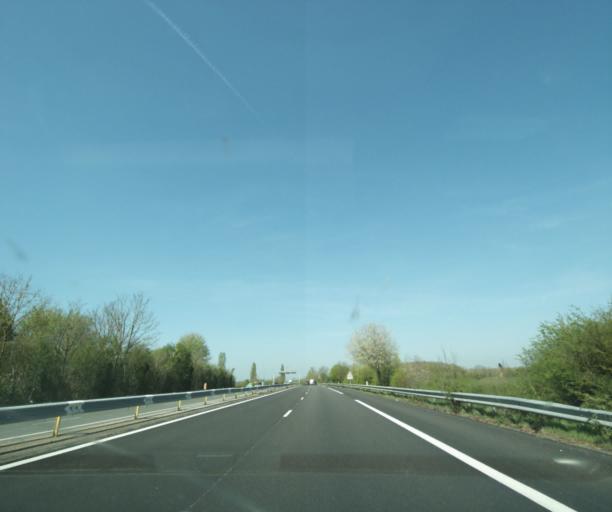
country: FR
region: Bourgogne
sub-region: Departement de la Nievre
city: La Charite-sur-Loire
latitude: 47.1907
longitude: 3.0315
